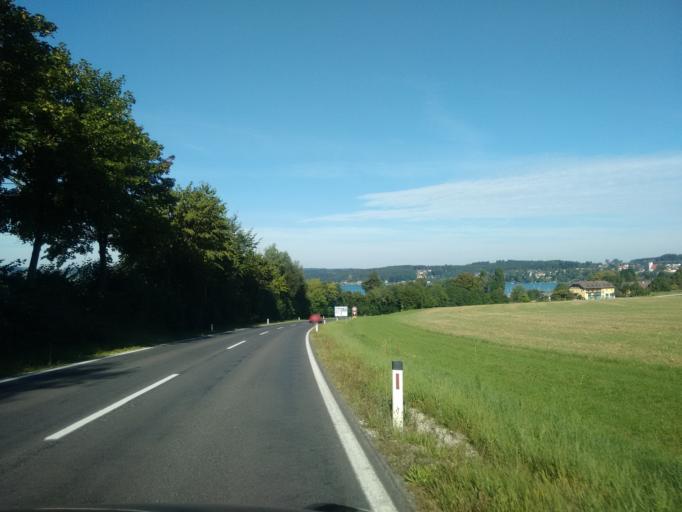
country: AT
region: Upper Austria
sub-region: Politischer Bezirk Vocklabruck
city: Seewalchen
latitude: 47.9379
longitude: 13.5992
